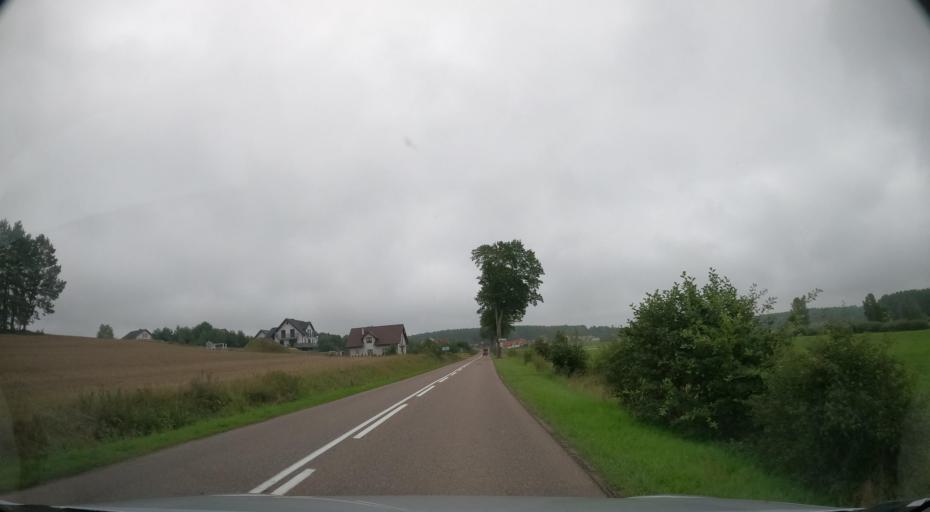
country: PL
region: Pomeranian Voivodeship
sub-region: Powiat wejherowski
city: Luzino
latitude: 54.4668
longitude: 18.0657
